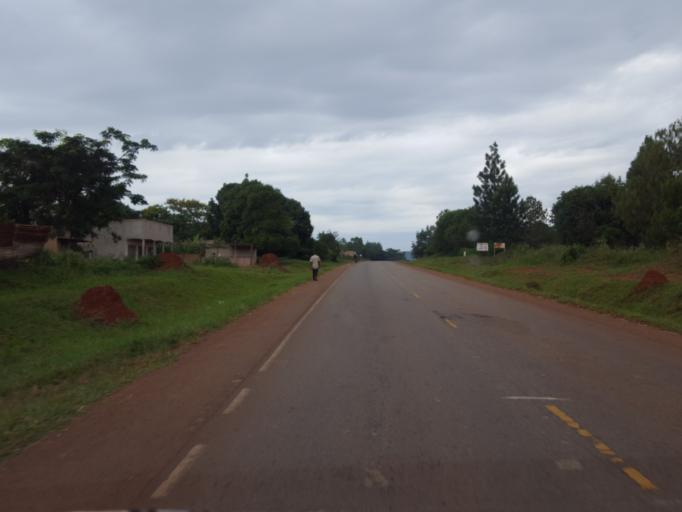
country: UG
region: Central Region
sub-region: Kiboga District
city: Kiboga
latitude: 1.0122
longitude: 31.6930
